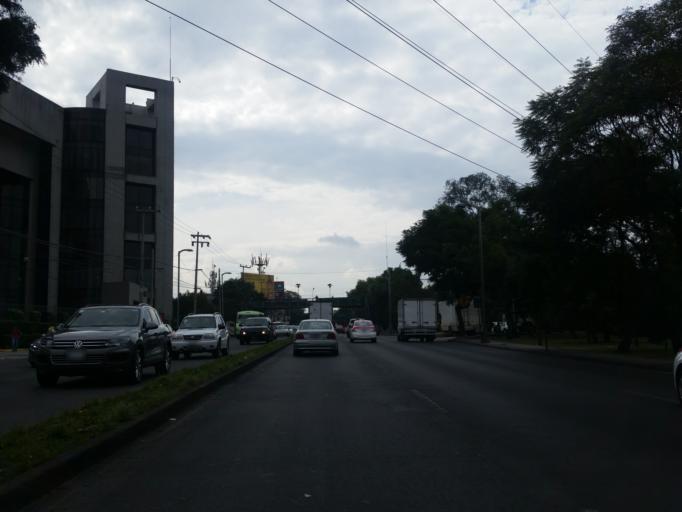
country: MX
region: Mexico City
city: Polanco
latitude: 19.3985
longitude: -99.2154
